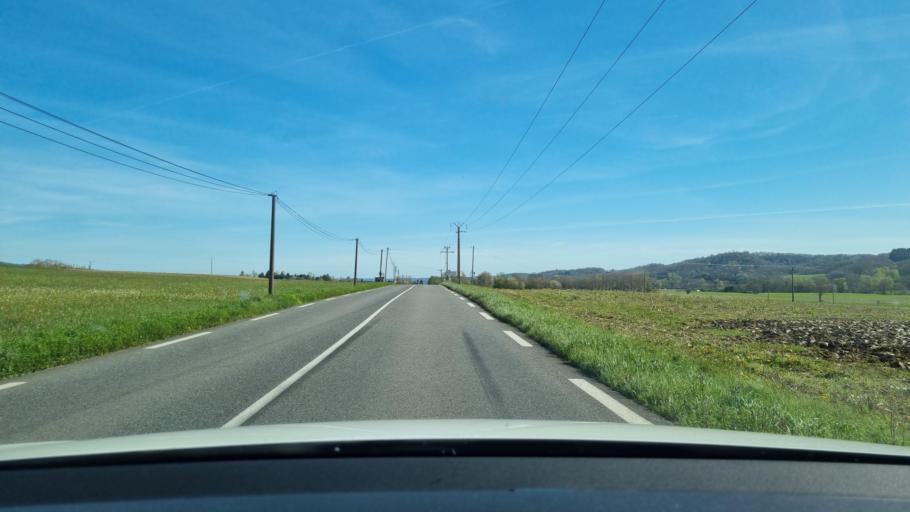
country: FR
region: Midi-Pyrenees
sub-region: Departement des Hautes-Pyrenees
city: Lannemezan
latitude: 43.2135
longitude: 0.4711
